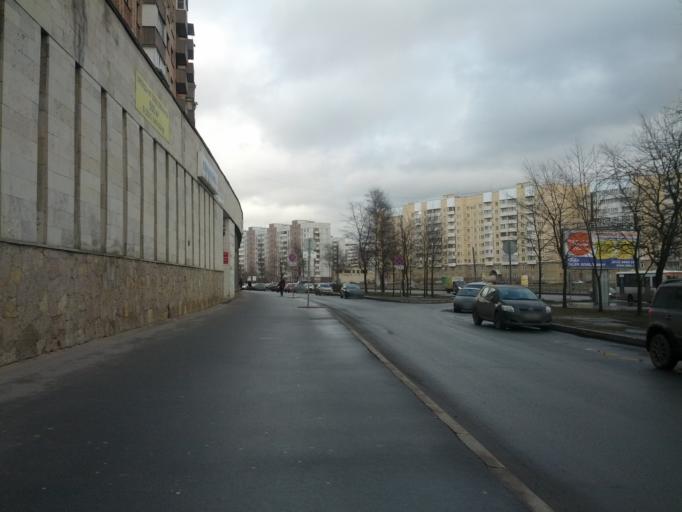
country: RU
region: Leningrad
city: Rybatskoye
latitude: 59.8955
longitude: 30.4909
